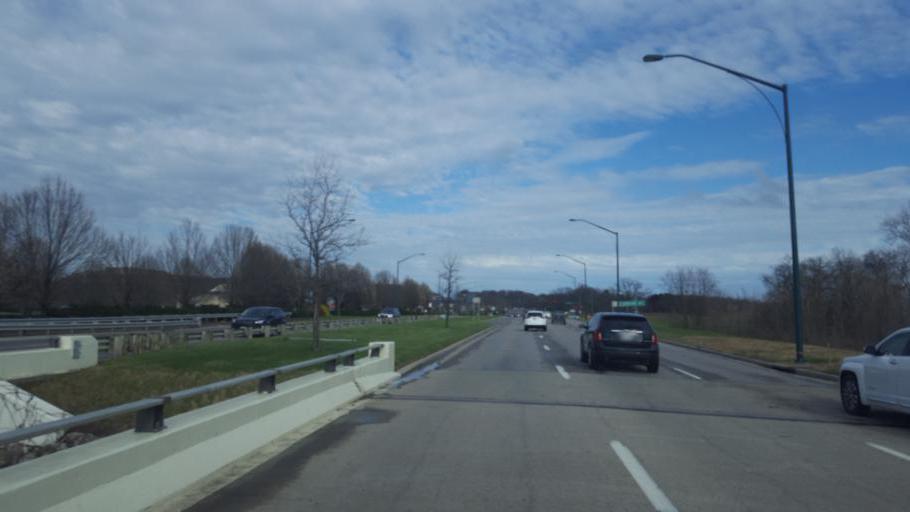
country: US
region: Ohio
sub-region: Franklin County
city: Westerville
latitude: 40.1458
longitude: -82.9497
